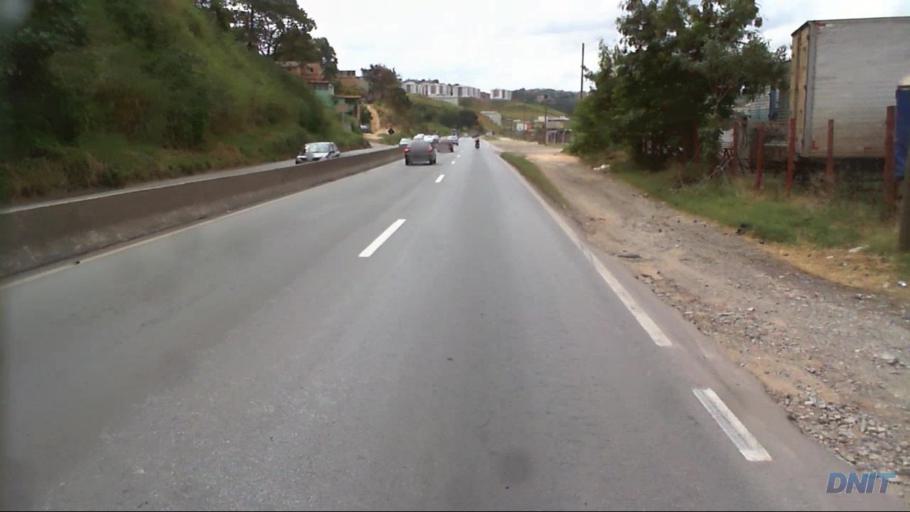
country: BR
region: Minas Gerais
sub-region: Belo Horizonte
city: Belo Horizonte
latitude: -19.8509
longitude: -43.8880
